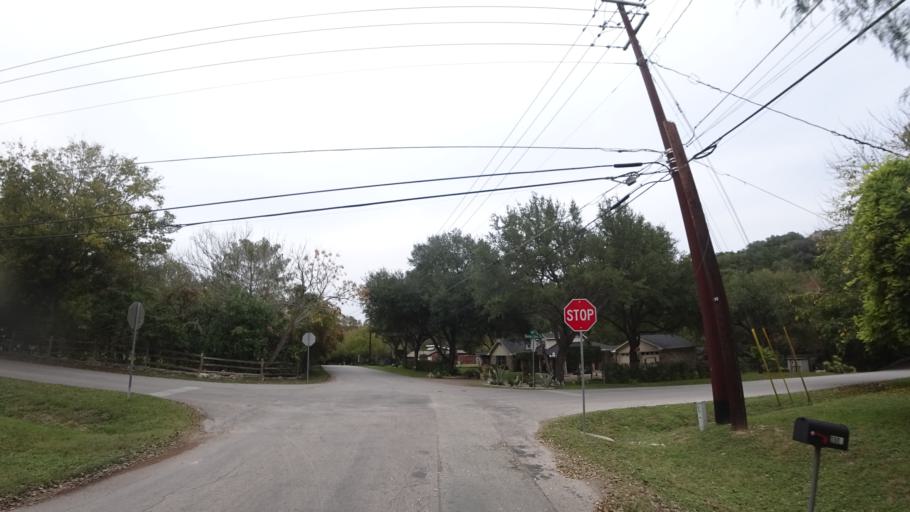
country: US
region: Texas
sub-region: Travis County
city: Hudson Bend
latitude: 30.3769
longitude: -97.9176
